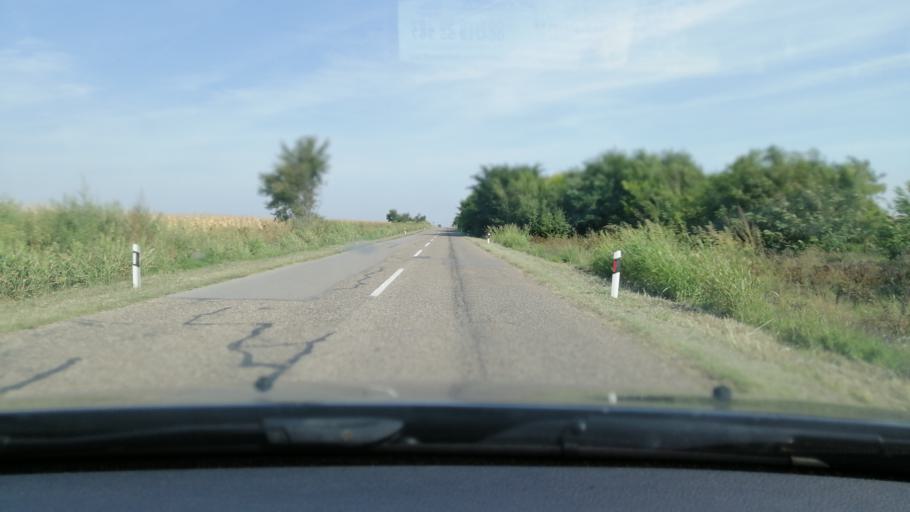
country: RS
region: Autonomna Pokrajina Vojvodina
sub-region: Juznobanatski Okrug
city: Kovacica
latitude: 45.1510
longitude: 20.6167
